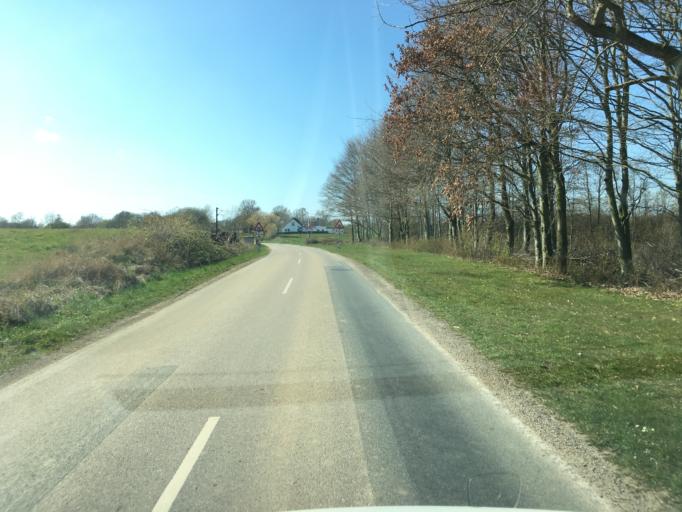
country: DK
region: South Denmark
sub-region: Sonderborg Kommune
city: Grasten
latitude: 54.9044
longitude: 9.5683
